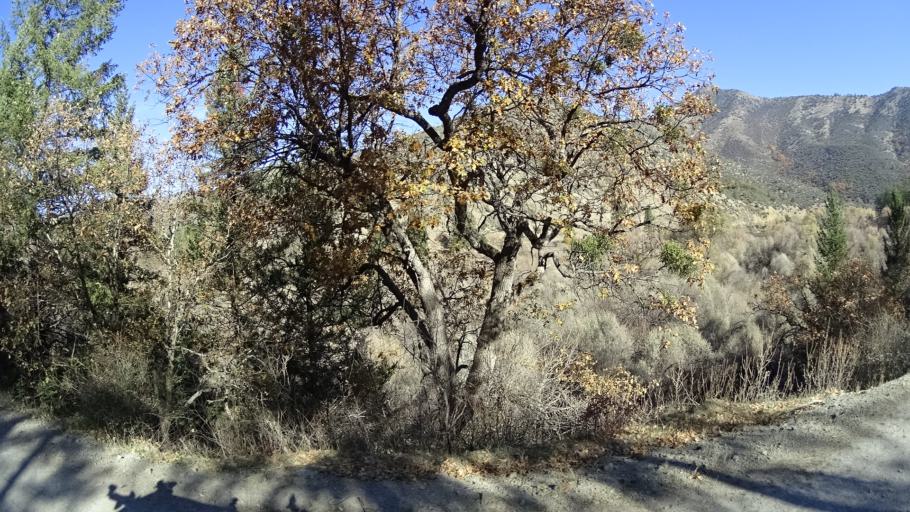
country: US
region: California
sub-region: Siskiyou County
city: Yreka
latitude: 41.8406
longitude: -122.6815
